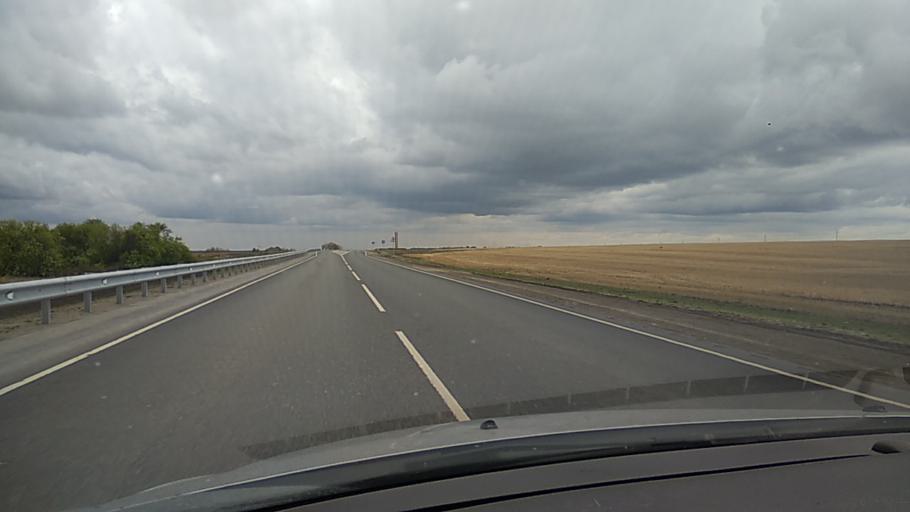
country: RU
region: Kurgan
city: Kataysk
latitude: 56.2879
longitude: 62.7513
